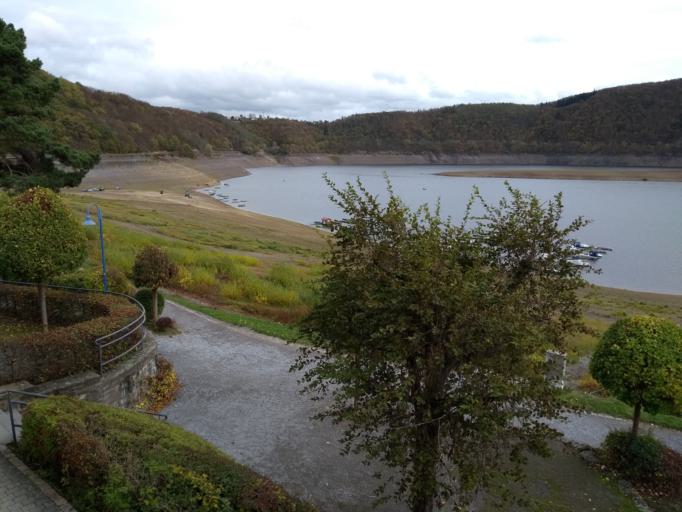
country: DE
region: Hesse
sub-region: Regierungsbezirk Kassel
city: Waldeck
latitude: 51.1998
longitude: 9.0470
